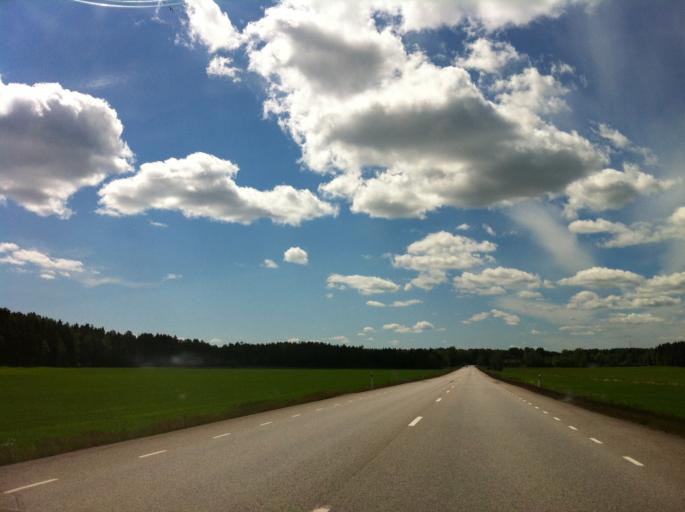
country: SE
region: Vaestra Goetaland
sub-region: Amals Kommun
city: Amal
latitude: 59.0123
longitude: 12.6913
